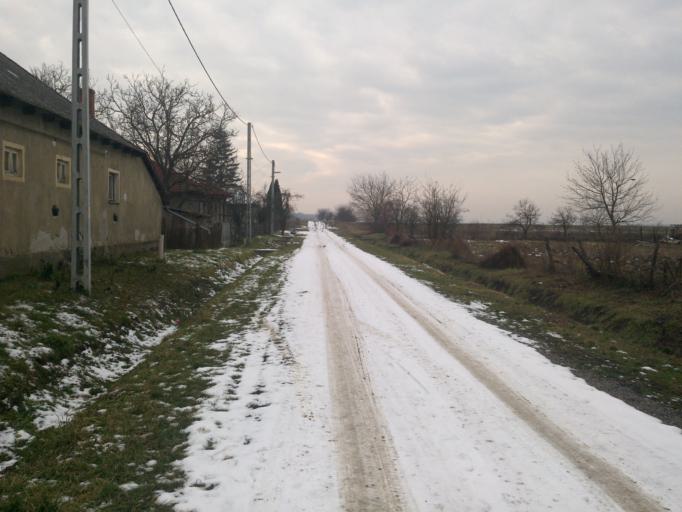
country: HU
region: Borsod-Abauj-Zemplen
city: Encs
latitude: 48.3175
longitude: 21.1570
